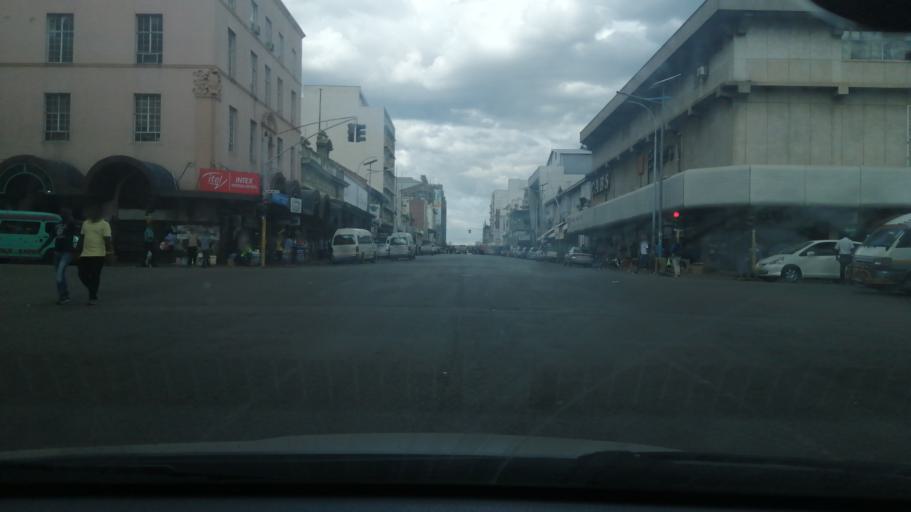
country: ZW
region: Harare
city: Harare
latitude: -17.8328
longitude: 31.0486
